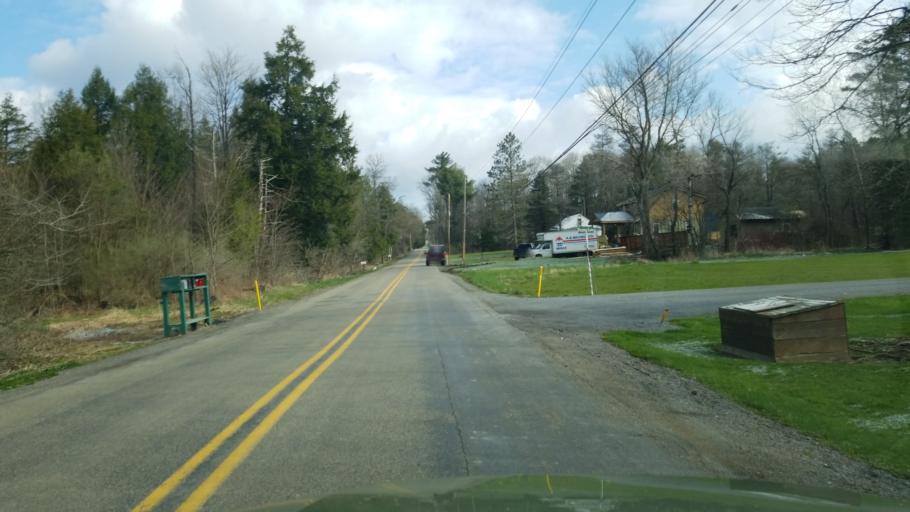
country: US
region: Pennsylvania
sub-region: Jefferson County
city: Brockway
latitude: 41.2519
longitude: -78.8383
